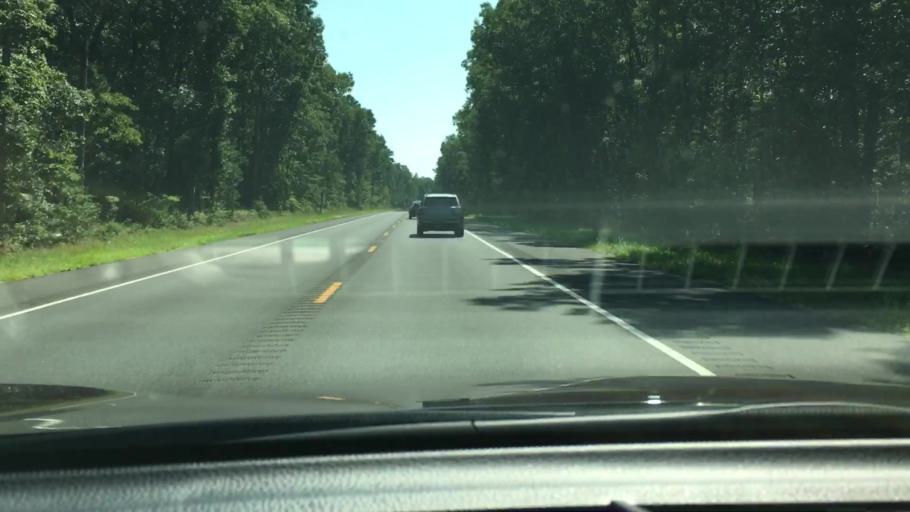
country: US
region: New Jersey
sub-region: Cape May County
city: Woodbine
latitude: 39.3168
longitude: -74.8392
